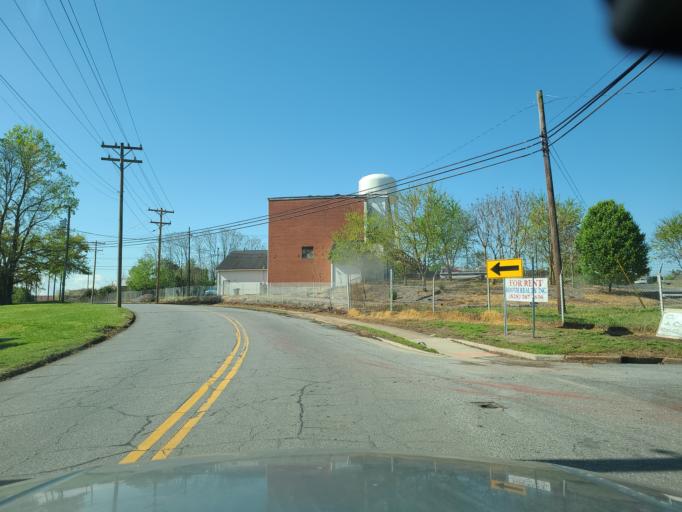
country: US
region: North Carolina
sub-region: Rutherford County
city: Spindale
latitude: 35.3622
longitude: -81.9296
